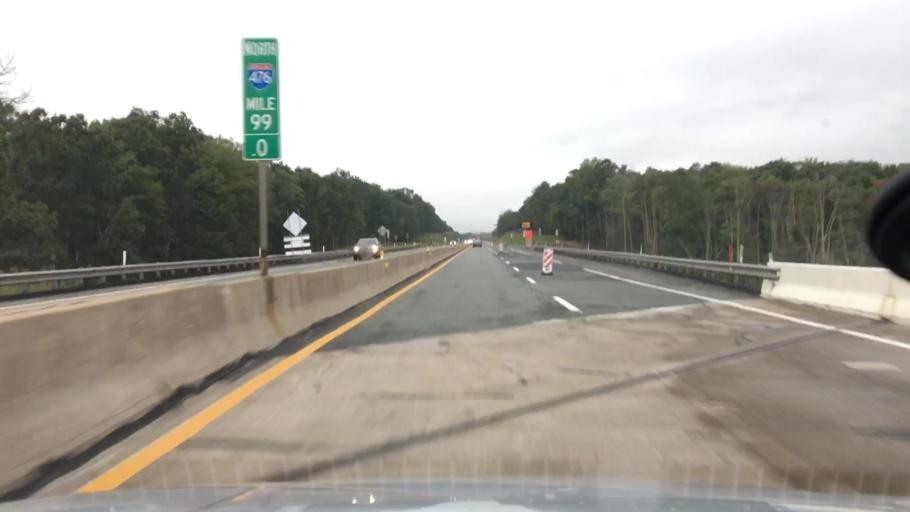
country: US
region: Pennsylvania
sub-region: Luzerne County
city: White Haven
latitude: 41.1149
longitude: -75.7614
